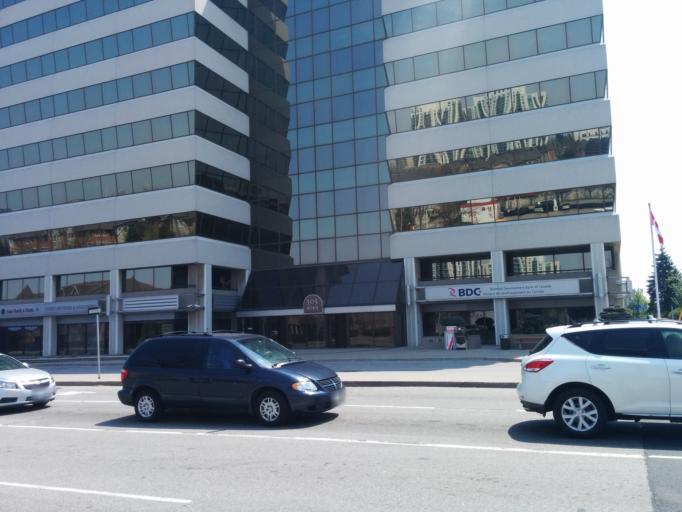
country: CA
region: Ontario
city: Scarborough
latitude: 43.7899
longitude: -79.2367
